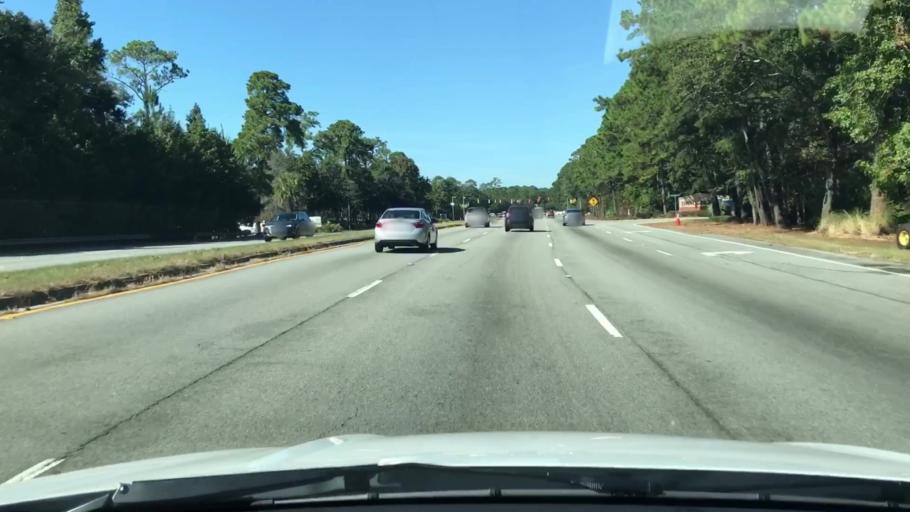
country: US
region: South Carolina
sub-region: Beaufort County
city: Bluffton
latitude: 32.2533
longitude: -80.8460
